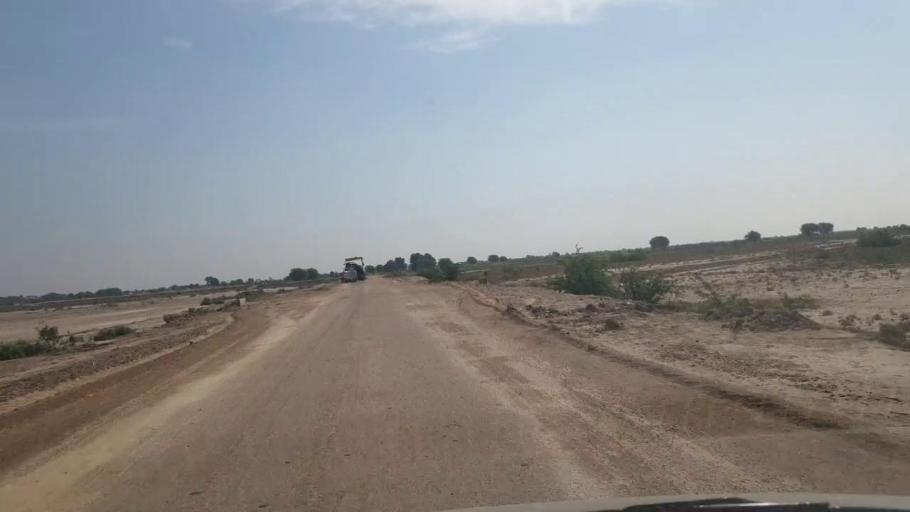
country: PK
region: Sindh
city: Digri
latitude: 24.9738
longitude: 69.1229
